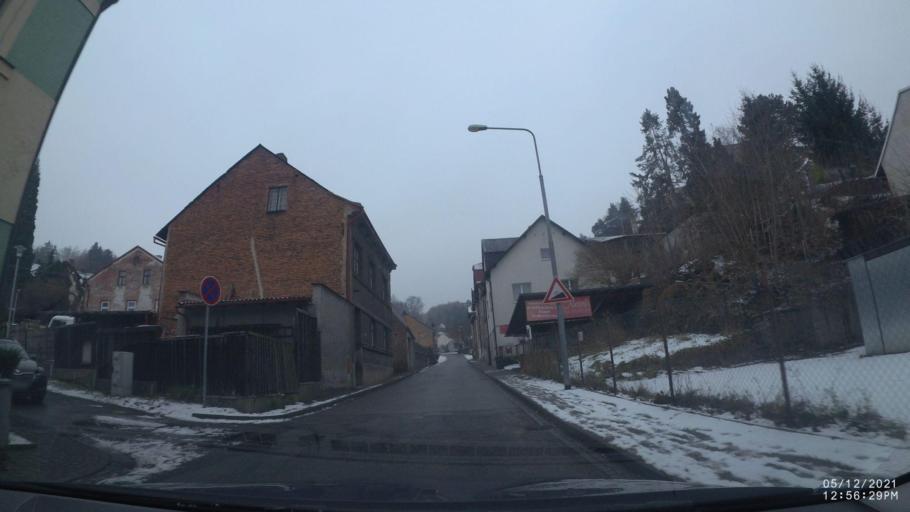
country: CZ
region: Kralovehradecky
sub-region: Okres Nachod
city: Nachod
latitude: 50.4168
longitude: 16.1579
